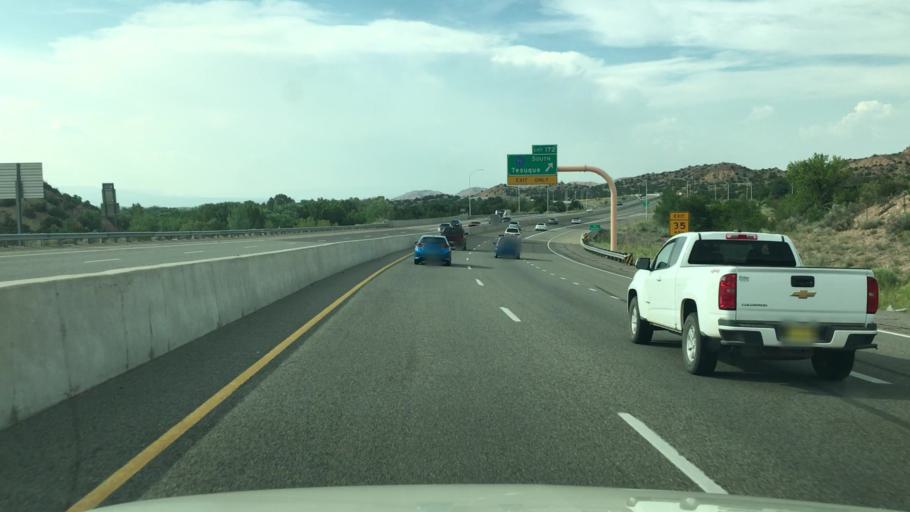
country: US
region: New Mexico
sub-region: Santa Fe County
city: Santa Fe
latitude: 35.7786
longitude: -105.9473
